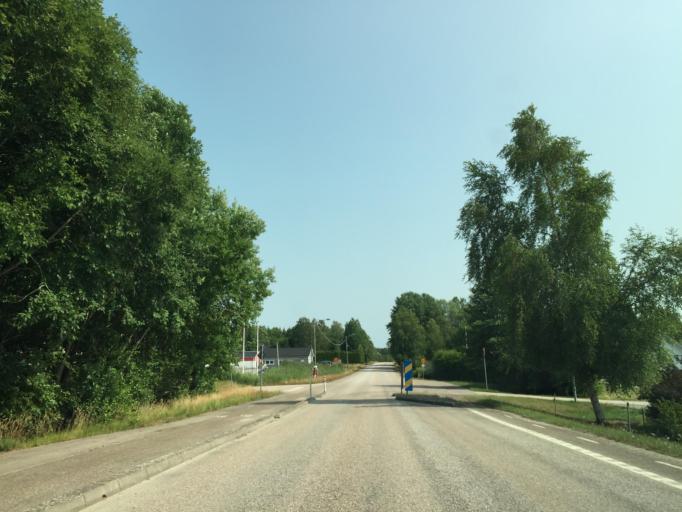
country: SE
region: Vaestra Goetaland
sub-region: Trollhattan
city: Sjuntorp
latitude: 58.3304
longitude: 12.1438
